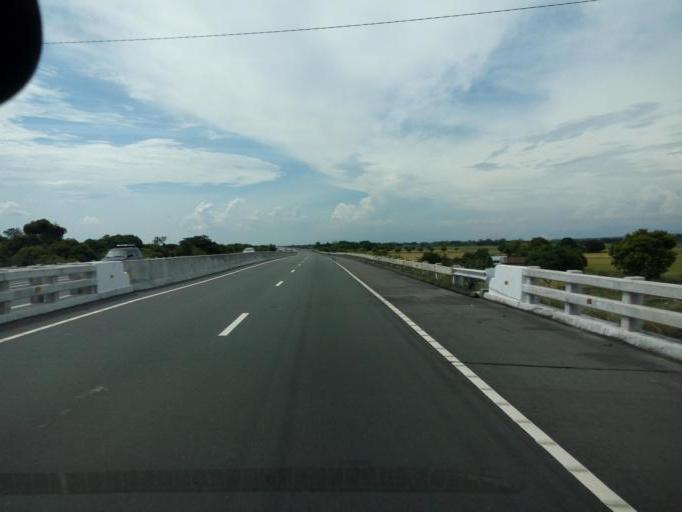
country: PH
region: Central Luzon
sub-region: Province of Nueva Ecija
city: Calancuasan Norte
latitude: 15.8023
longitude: 120.6400
